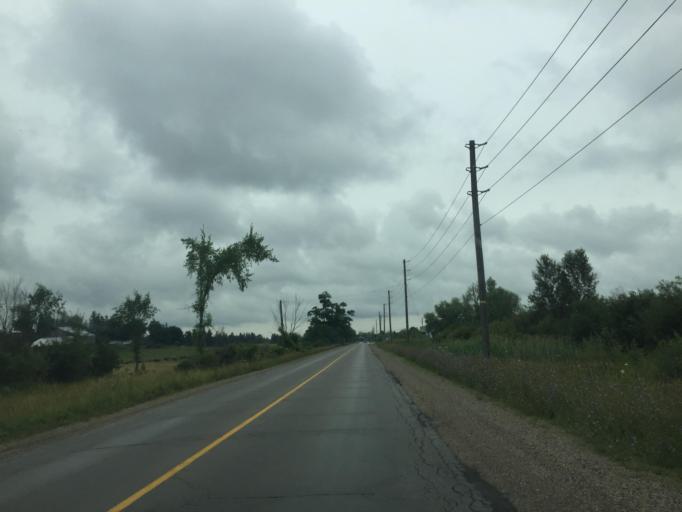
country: CA
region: Ontario
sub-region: Wellington County
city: Guelph
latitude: 43.4897
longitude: -80.2310
